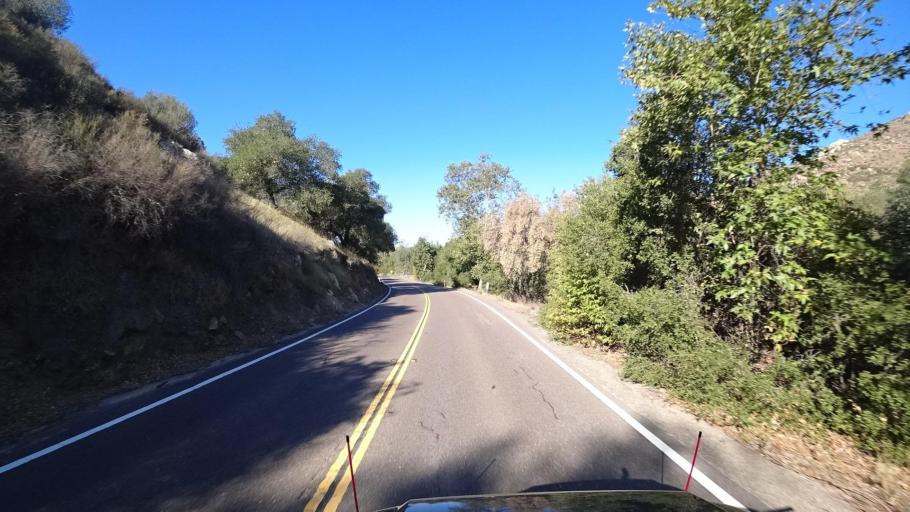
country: US
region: California
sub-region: San Diego County
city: Jamul
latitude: 32.6545
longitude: -116.7959
